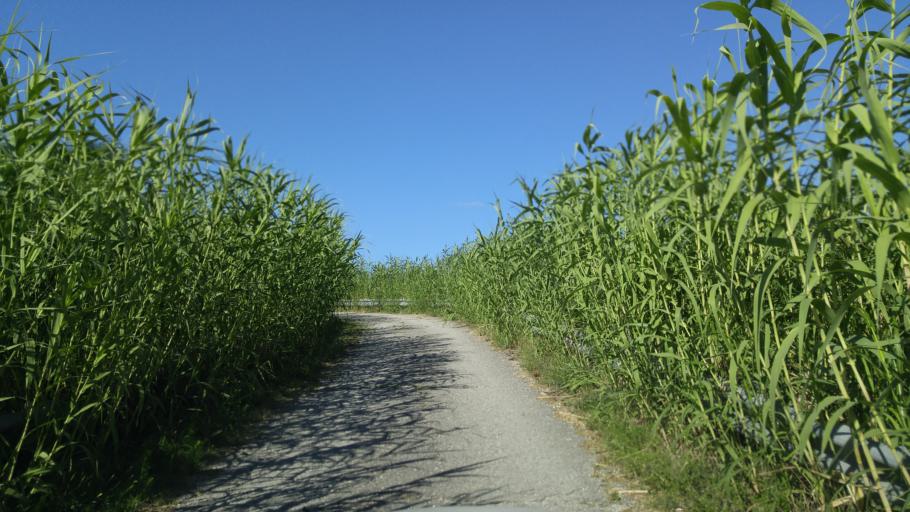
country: IT
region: The Marches
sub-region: Provincia di Pesaro e Urbino
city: Calcinelli
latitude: 43.7518
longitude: 12.9274
